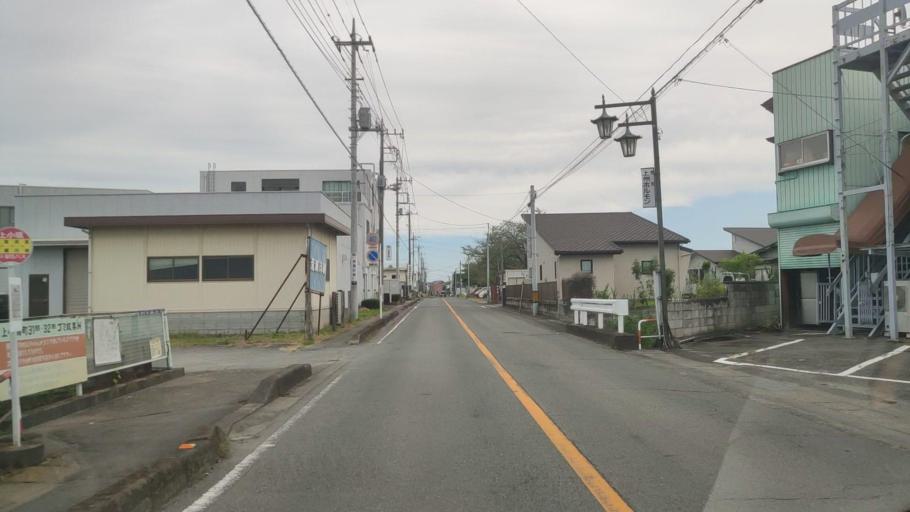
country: JP
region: Gunma
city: Takasaki
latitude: 36.3608
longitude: 138.9837
